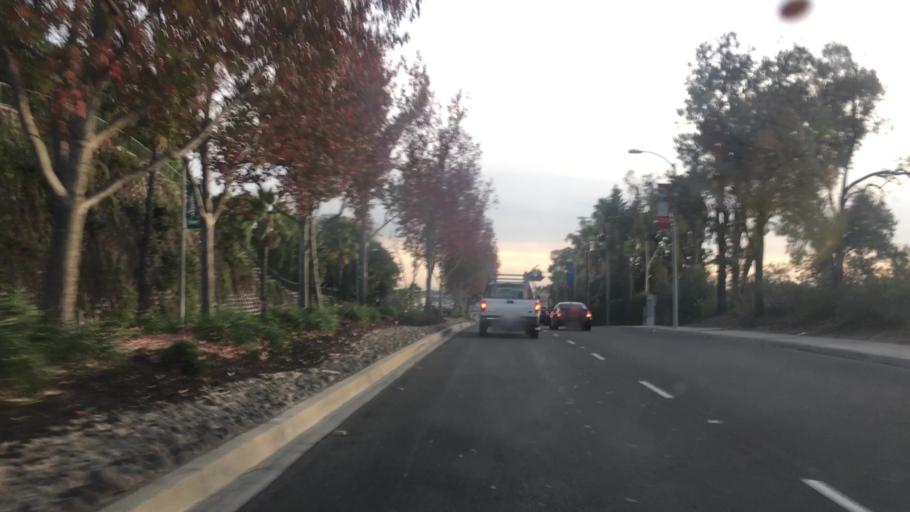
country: US
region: California
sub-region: Los Angeles County
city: Signal Hill
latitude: 33.7995
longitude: -118.1677
